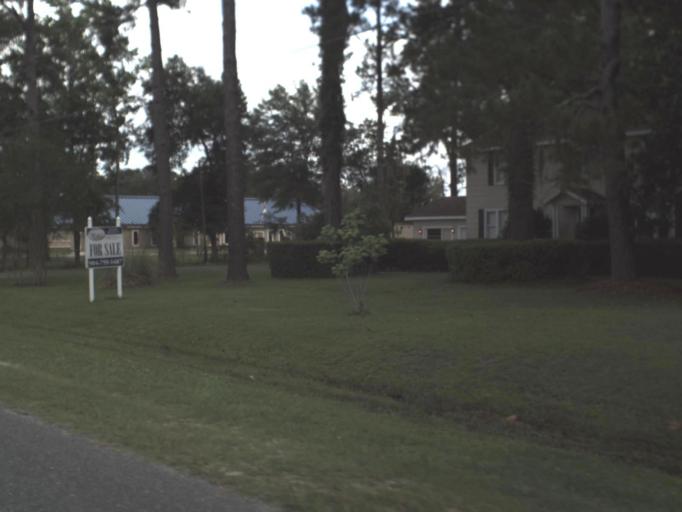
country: US
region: Florida
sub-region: Nassau County
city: Callahan
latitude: 30.5495
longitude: -81.8194
